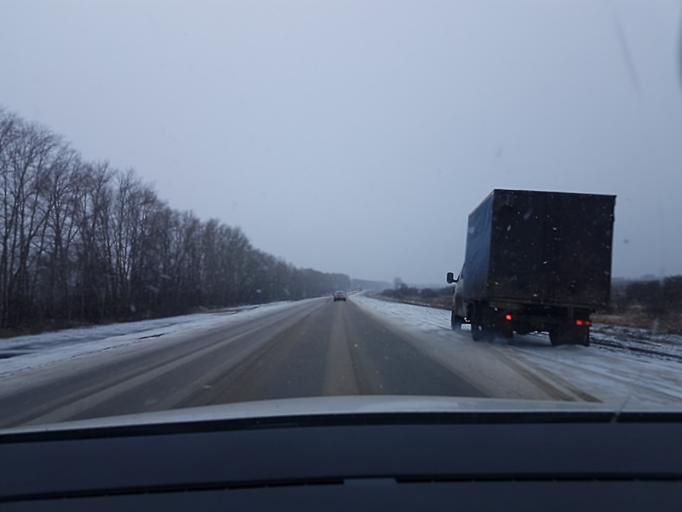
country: RU
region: Tambov
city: Pervomayskiy
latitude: 53.2679
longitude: 40.2289
